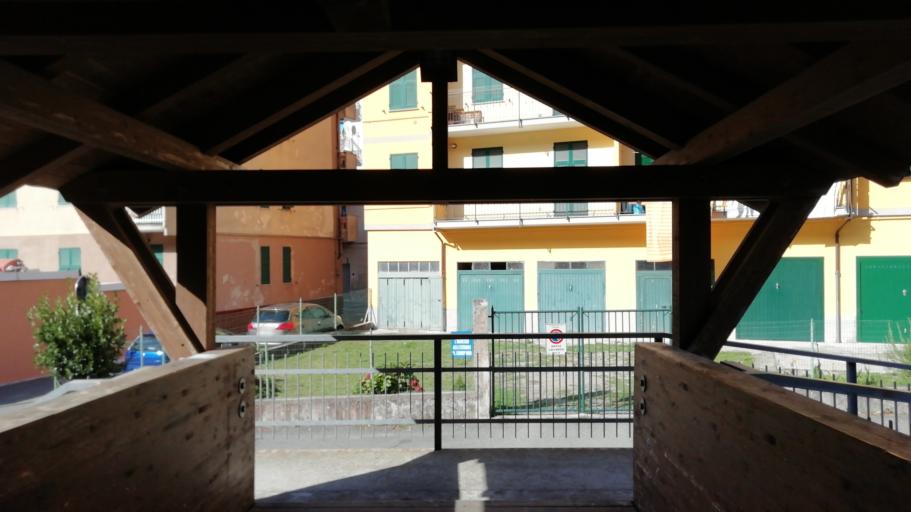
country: IT
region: Liguria
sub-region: Provincia di Genova
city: Masone
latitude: 44.5010
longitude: 8.7145
